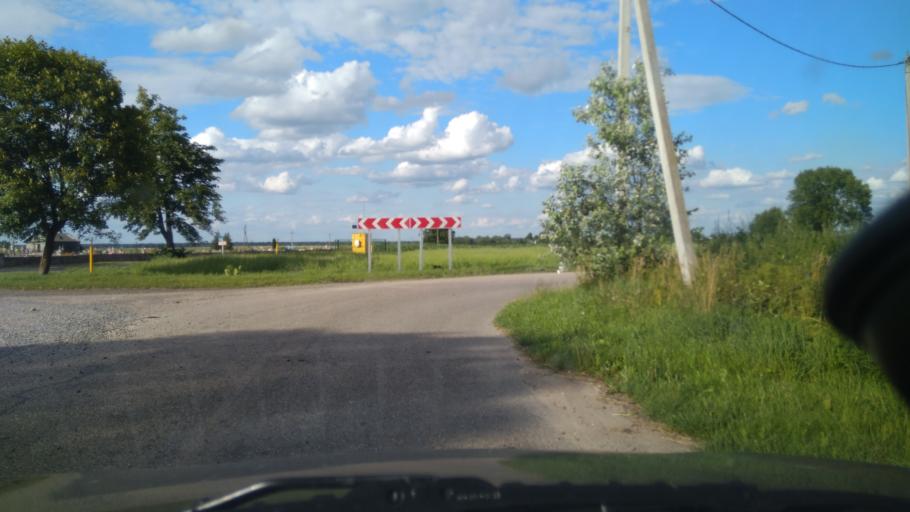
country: BY
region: Grodnenskaya
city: Masty
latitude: 53.3137
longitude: 24.7003
